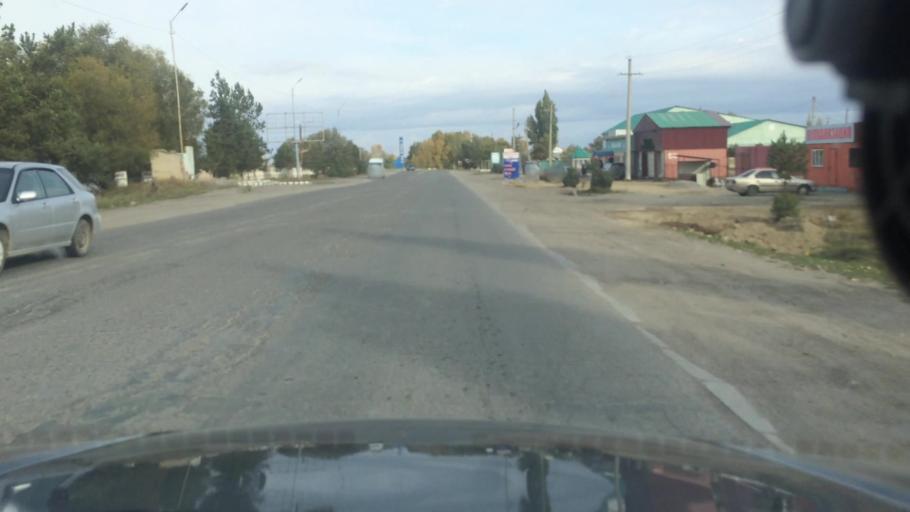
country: KG
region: Ysyk-Koel
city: Karakol
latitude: 42.5298
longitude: 78.3831
